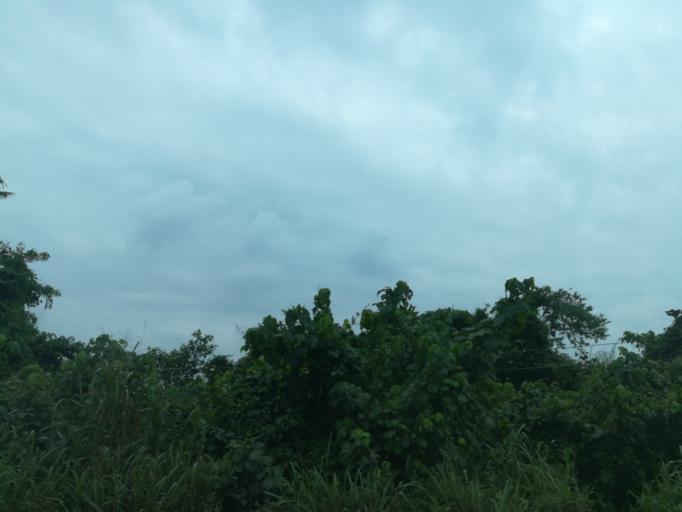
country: NG
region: Lagos
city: Ejirin
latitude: 6.6467
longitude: 3.7704
